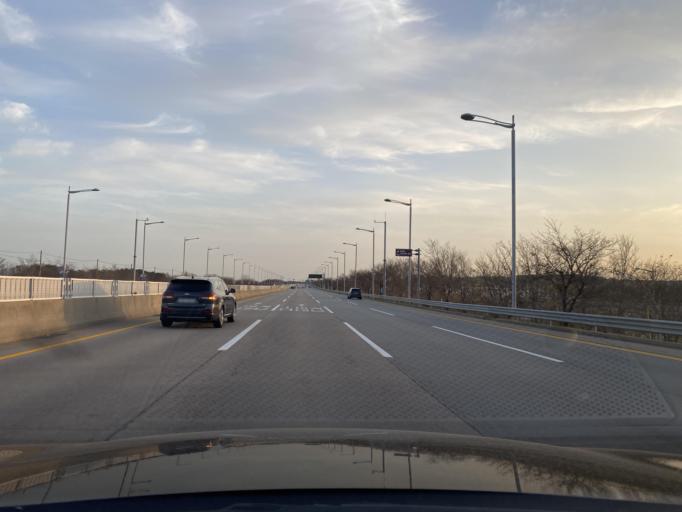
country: KR
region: Incheon
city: Incheon
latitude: 37.4702
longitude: 126.4860
